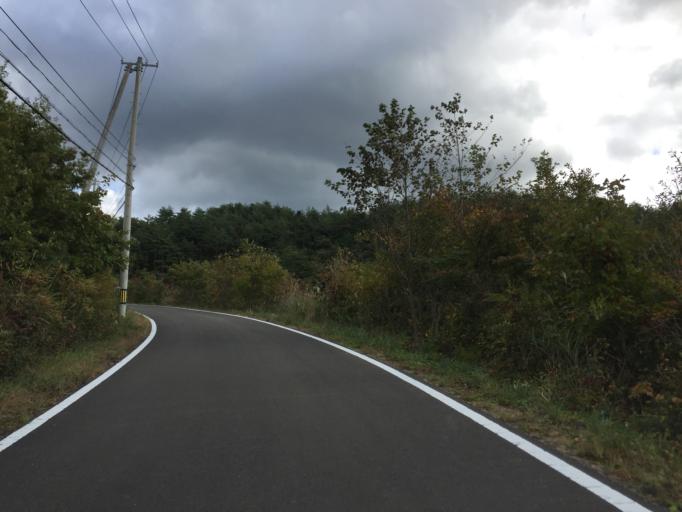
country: JP
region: Miyagi
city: Marumori
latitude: 37.8128
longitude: 140.7729
